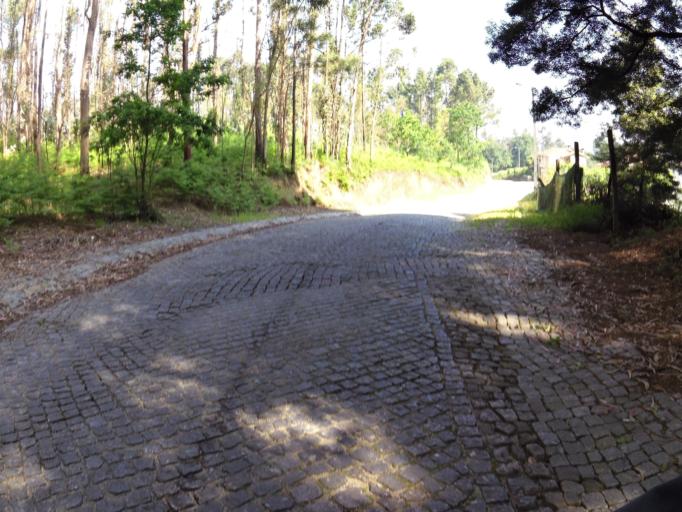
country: PT
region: Porto
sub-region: Vila Nova de Gaia
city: Olival
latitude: 41.0428
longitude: -8.5353
